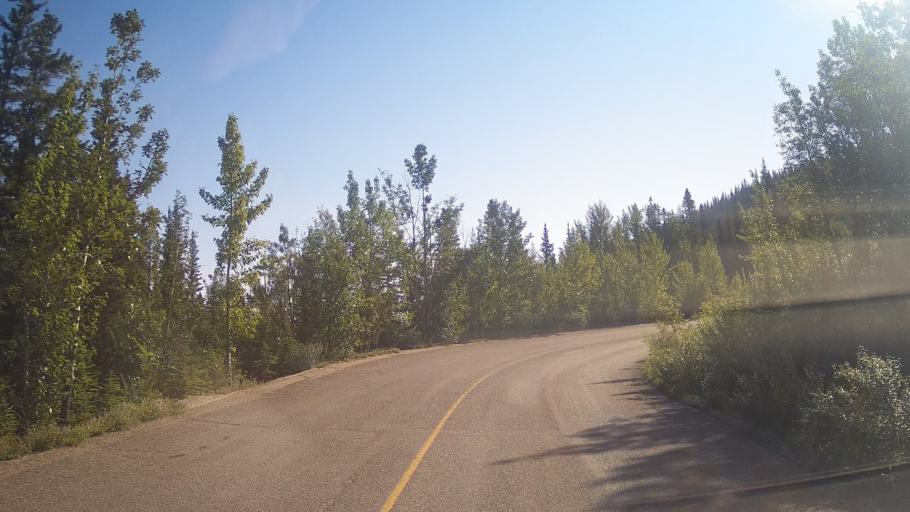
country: CA
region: Alberta
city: Jasper Park Lodge
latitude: 53.2049
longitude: -117.9227
